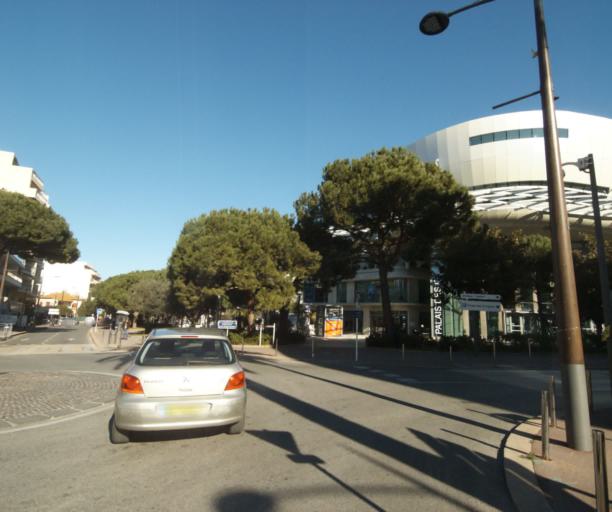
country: FR
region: Provence-Alpes-Cote d'Azur
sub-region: Departement des Alpes-Maritimes
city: Antibes
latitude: 43.5678
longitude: 7.1156
